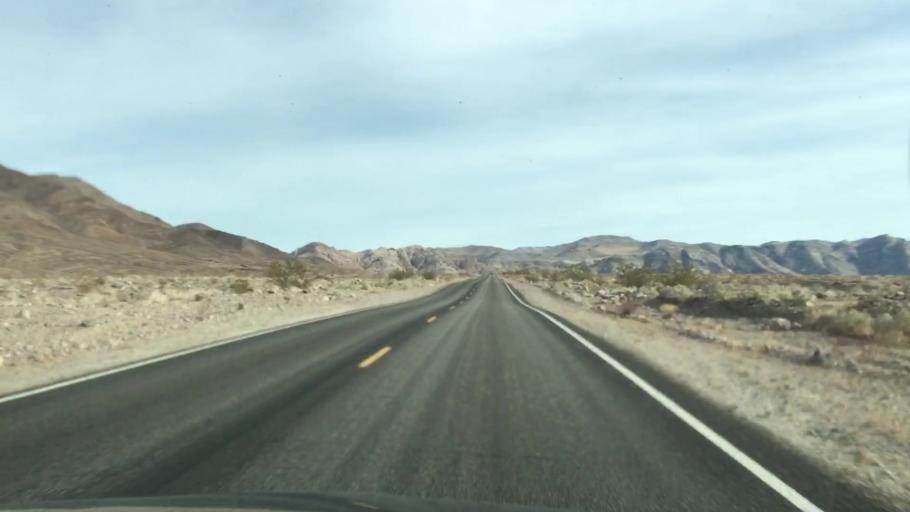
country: US
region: Nevada
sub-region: Nye County
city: Beatty
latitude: 36.7067
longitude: -116.9914
